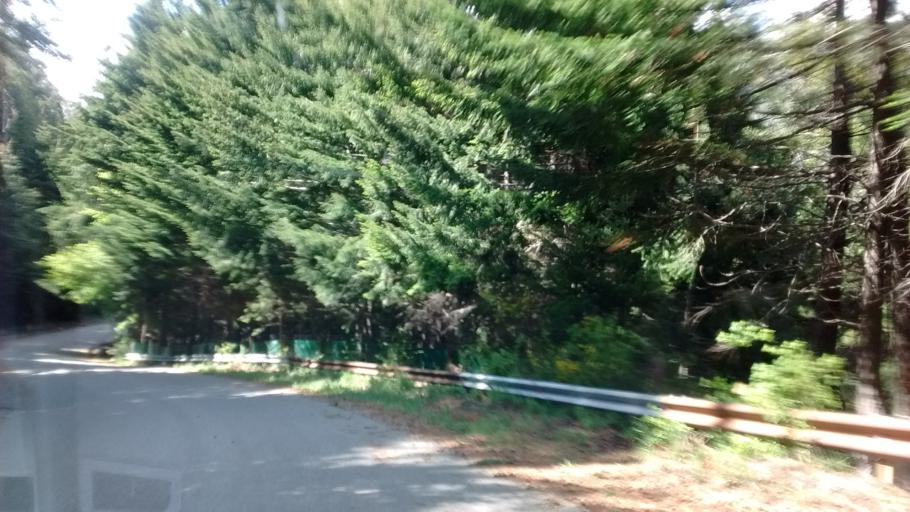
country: AR
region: Rio Negro
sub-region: Departamento de Bariloche
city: San Carlos de Bariloche
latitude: -41.0767
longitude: -71.5458
